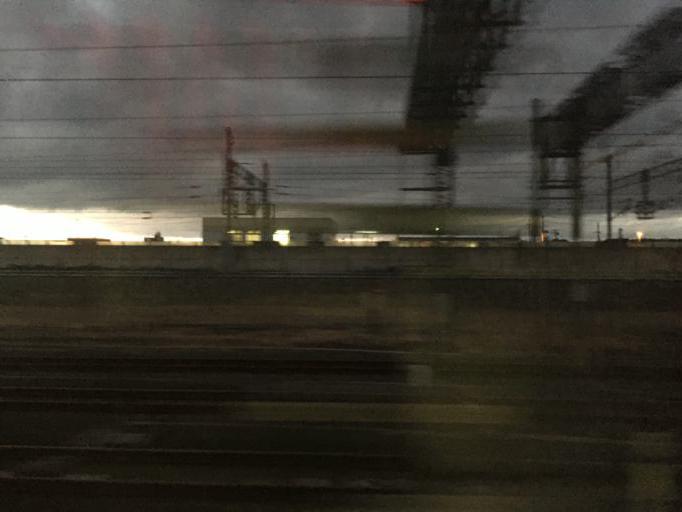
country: JP
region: Aomori
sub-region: Hachinohe Shi
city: Uchimaru
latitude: 40.5114
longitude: 141.4336
